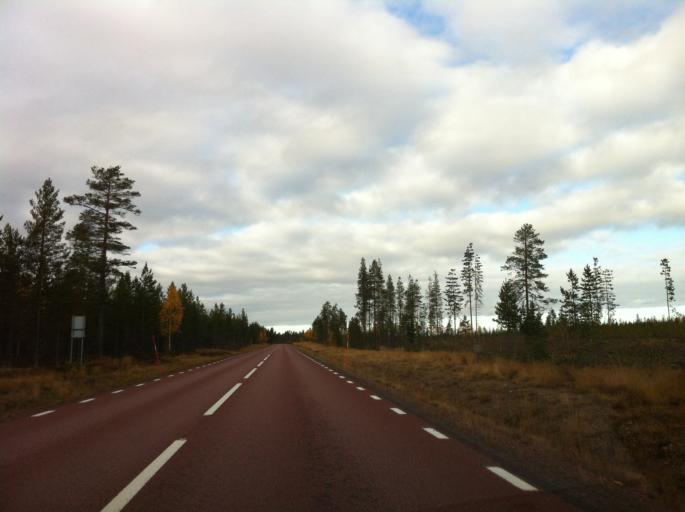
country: SE
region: Dalarna
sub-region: Alvdalens Kommun
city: AElvdalen
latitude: 61.5483
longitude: 13.3324
